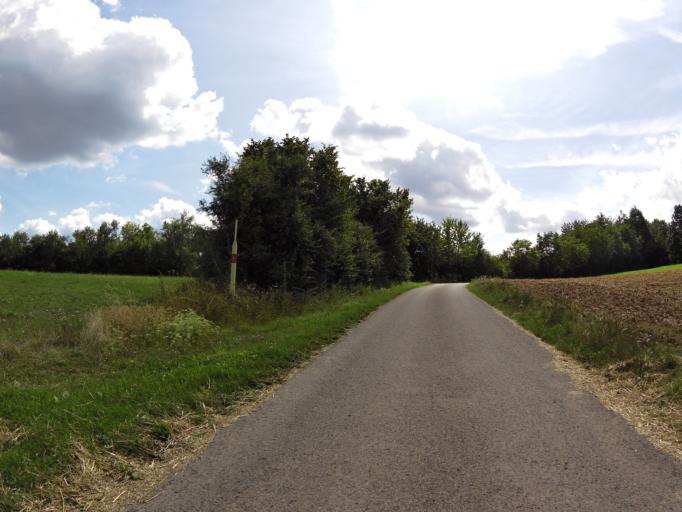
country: DE
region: Bavaria
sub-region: Regierungsbezirk Unterfranken
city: Margetshochheim
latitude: 49.8402
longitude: 9.8497
